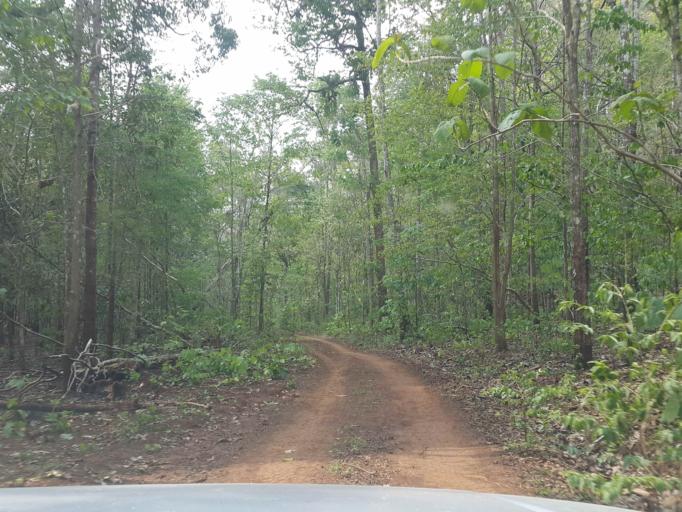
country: TH
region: Chiang Mai
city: Wiang Haeng
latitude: 19.3325
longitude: 98.7191
